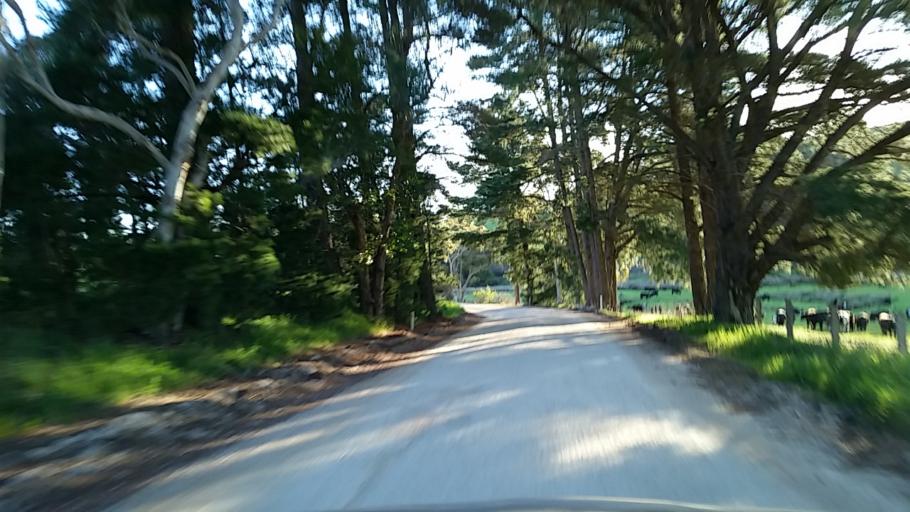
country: AU
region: South Australia
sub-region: Alexandrina
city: Mount Compass
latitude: -35.2888
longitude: 138.6909
